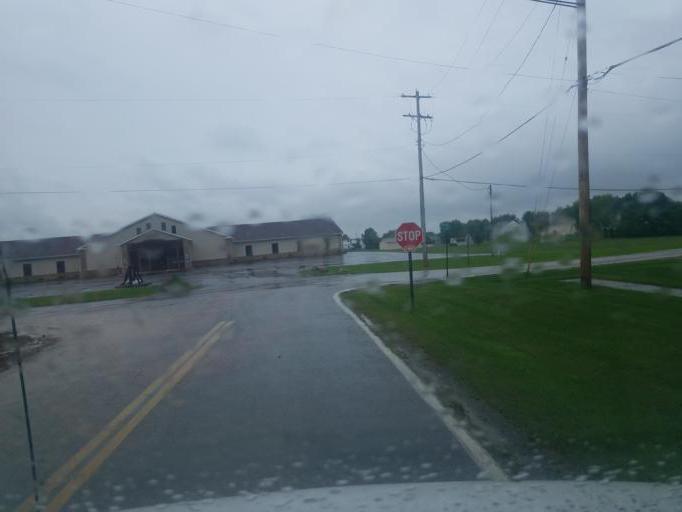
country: US
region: Ohio
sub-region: Wayne County
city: Rittman
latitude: 40.9836
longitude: -81.7987
